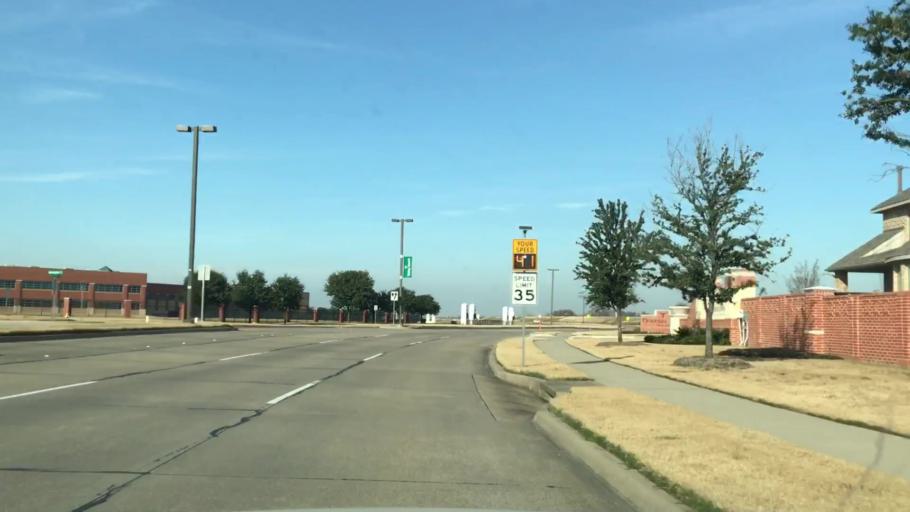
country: US
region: Texas
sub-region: Dallas County
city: Farmers Branch
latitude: 32.9159
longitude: -96.9440
